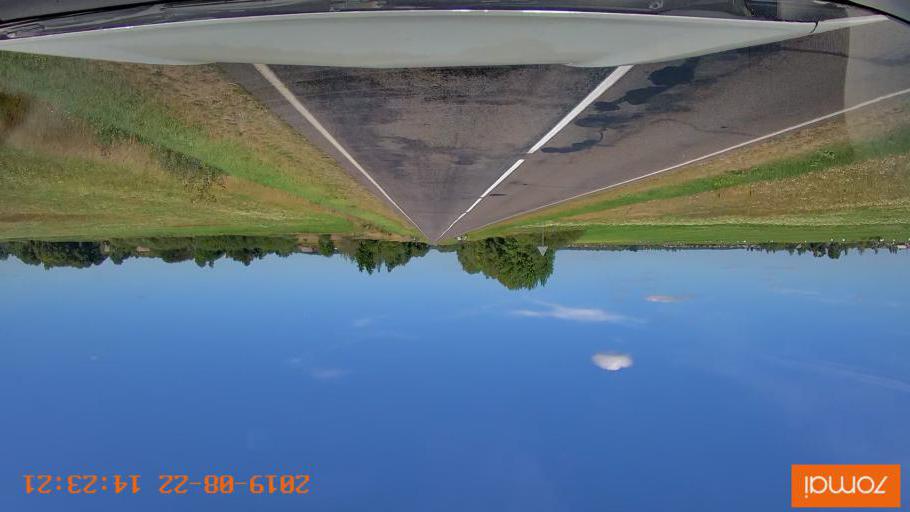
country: BY
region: Mogilev
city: Asipovichy
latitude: 53.2881
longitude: 28.5822
